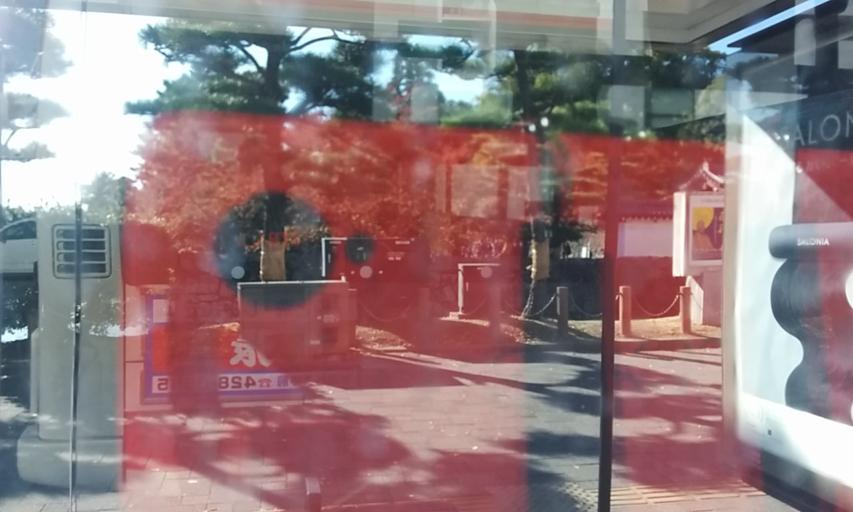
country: JP
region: Wakayama
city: Wakayama-shi
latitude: 34.2297
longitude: 135.1741
